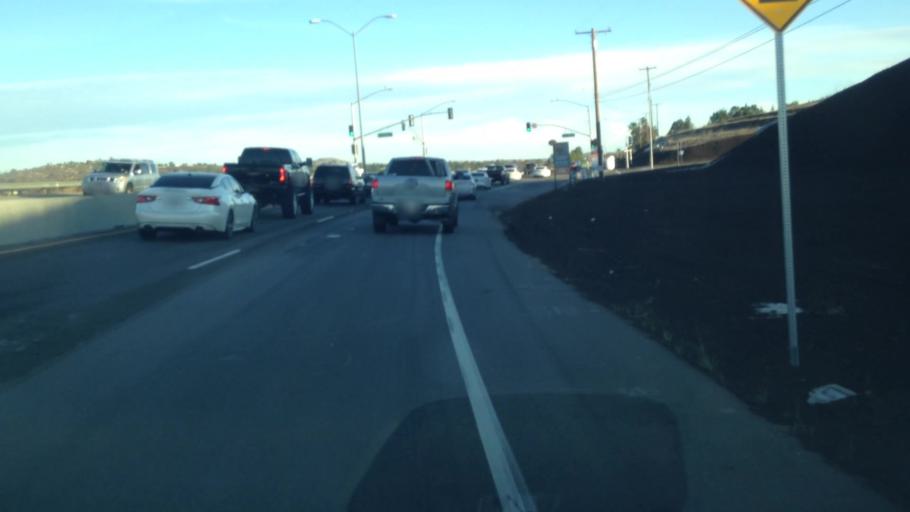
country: US
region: California
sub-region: Riverside County
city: Riverside
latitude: 33.8938
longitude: -117.4207
